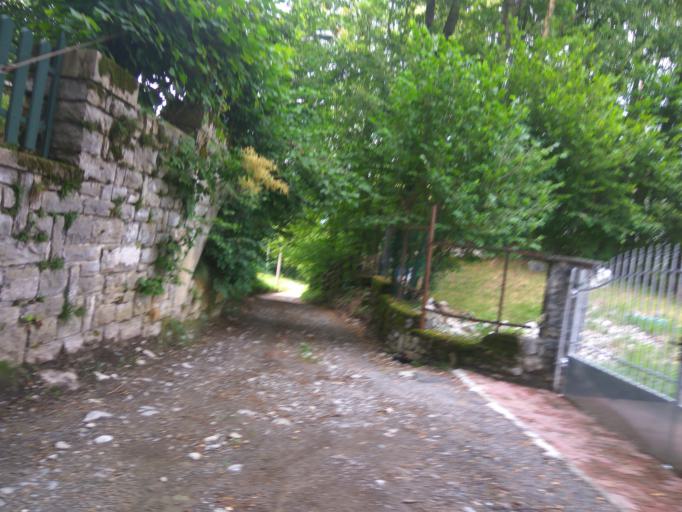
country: IT
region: Lombardy
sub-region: Provincia di Como
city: Lanzo d'Intelvi
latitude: 45.9898
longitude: 9.0295
